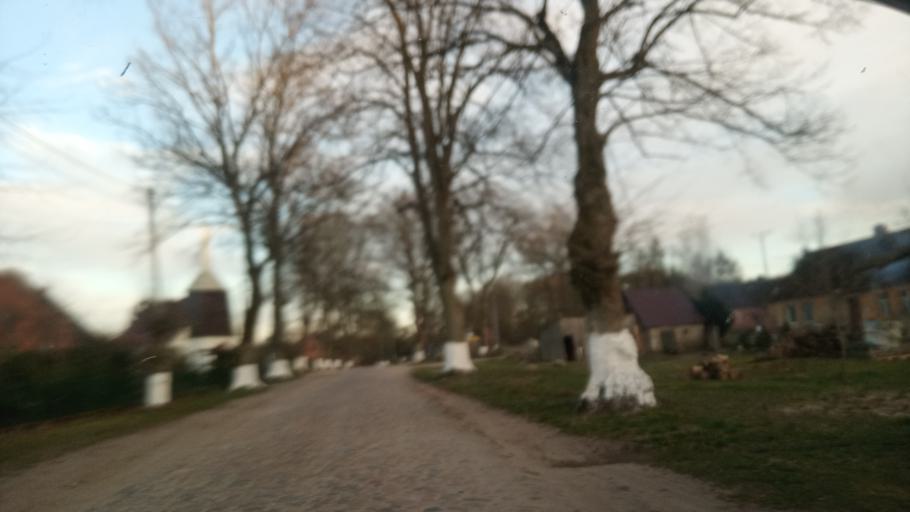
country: PL
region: West Pomeranian Voivodeship
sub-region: Powiat szczecinecki
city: Lubowo
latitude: 53.5517
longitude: 16.3933
